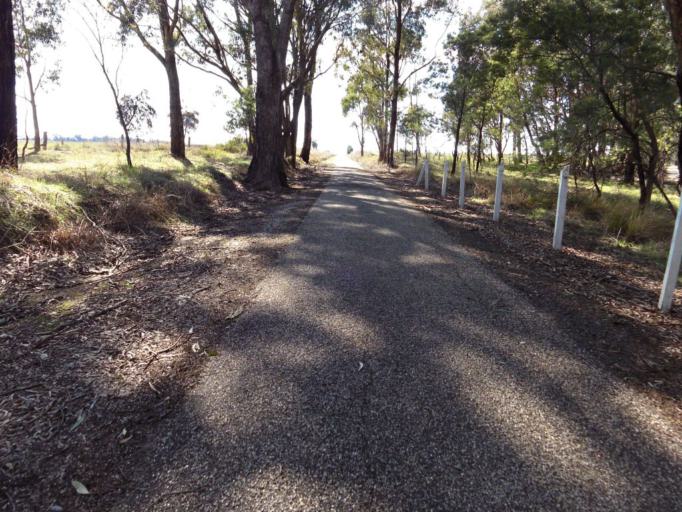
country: AU
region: Victoria
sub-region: Wangaratta
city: Wangaratta
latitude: -36.3992
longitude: 146.6482
